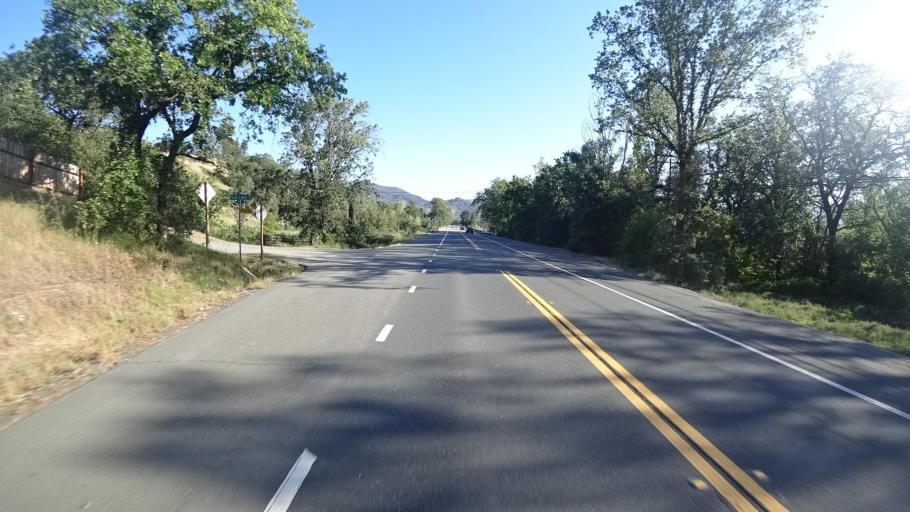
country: US
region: California
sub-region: Lake County
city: Upper Lake
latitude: 39.1564
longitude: -122.9209
